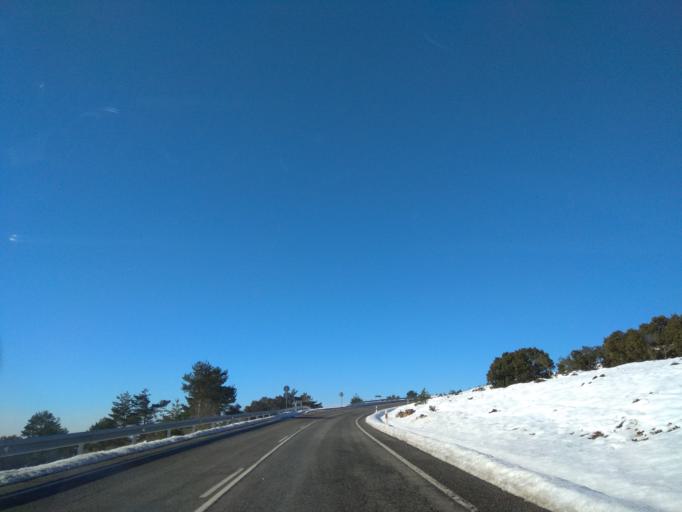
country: ES
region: Castille and Leon
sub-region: Provincia de Burgos
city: Medina de Pomar
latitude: 42.9374
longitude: -3.6683
